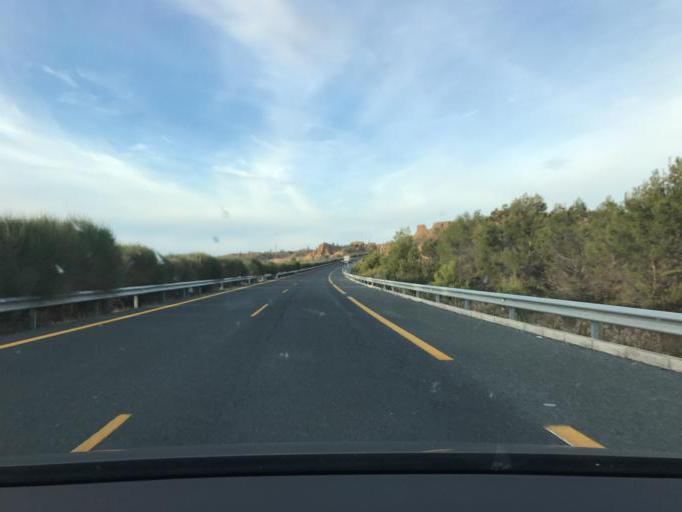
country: ES
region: Andalusia
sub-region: Provincia de Granada
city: Guadix
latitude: 37.3058
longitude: -3.1117
